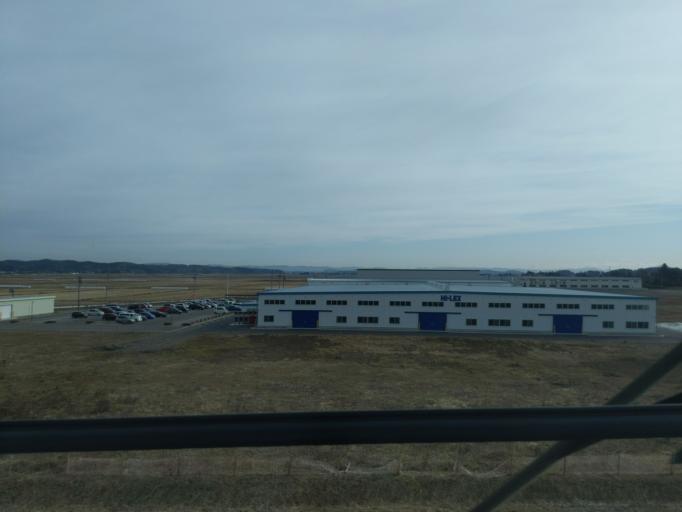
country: JP
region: Iwate
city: Ichinoseki
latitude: 38.7908
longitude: 141.0937
